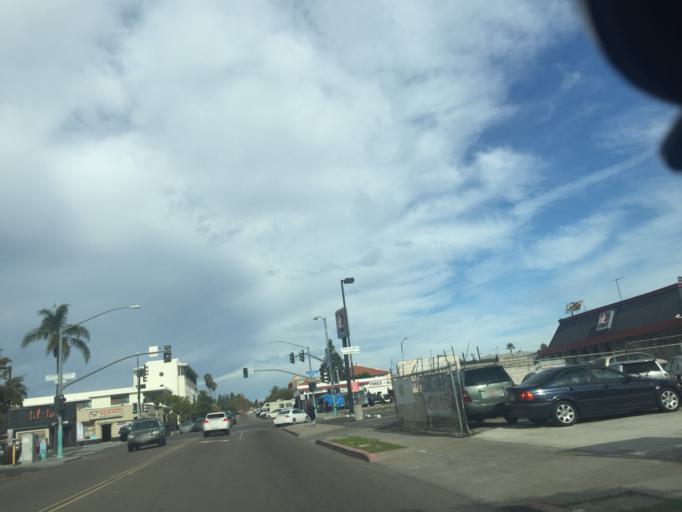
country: US
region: California
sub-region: San Diego County
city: Lemon Grove
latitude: 32.7554
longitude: -117.0922
